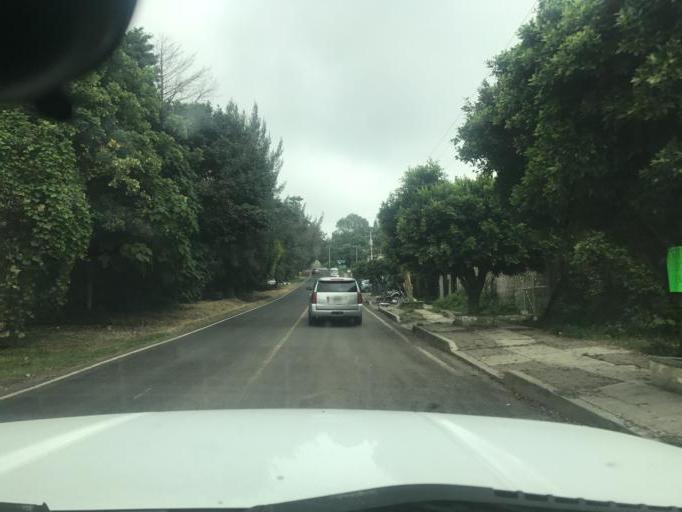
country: MX
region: Morelos
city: Ocuituco
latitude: 18.8807
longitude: -98.7738
